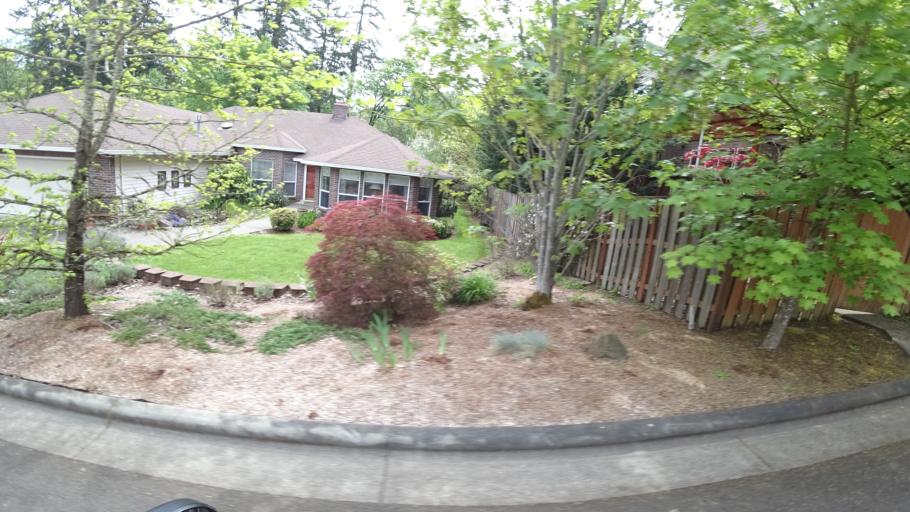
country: US
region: Oregon
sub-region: Washington County
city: Aloha
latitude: 45.4627
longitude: -122.8581
